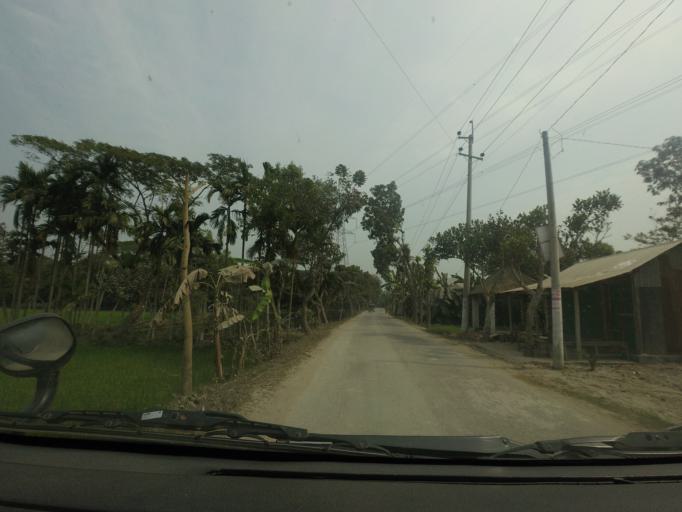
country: BD
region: Dhaka
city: Kishorganj
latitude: 24.3438
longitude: 90.7750
